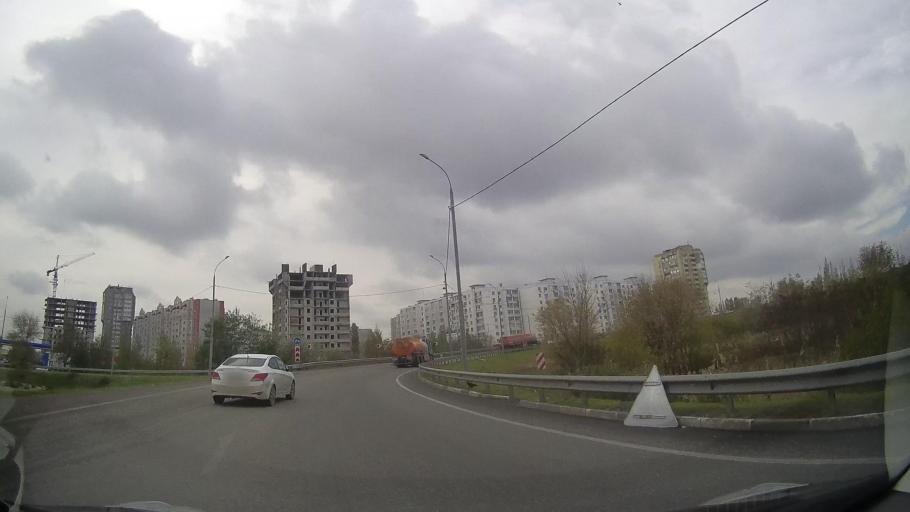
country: RU
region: Rostov
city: Bataysk
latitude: 47.1580
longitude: 39.7432
